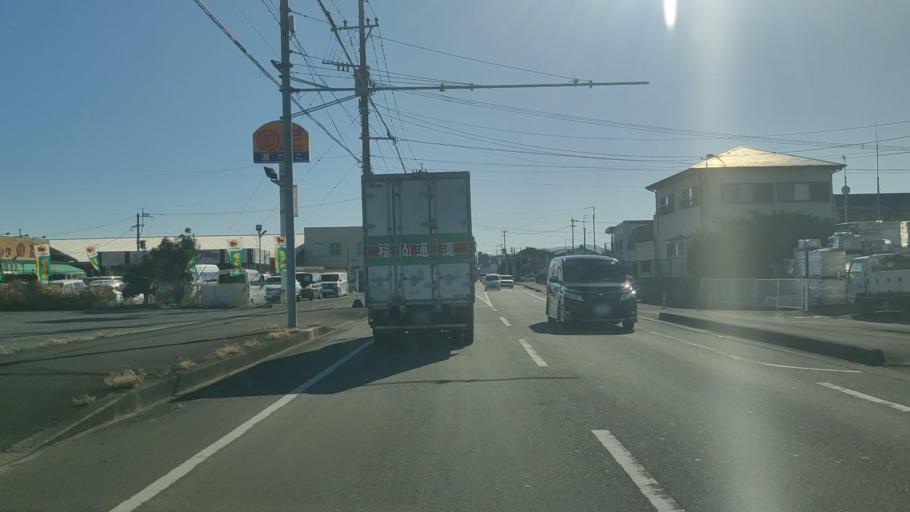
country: JP
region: Miyazaki
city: Miyazaki-shi
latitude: 31.9412
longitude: 131.4572
